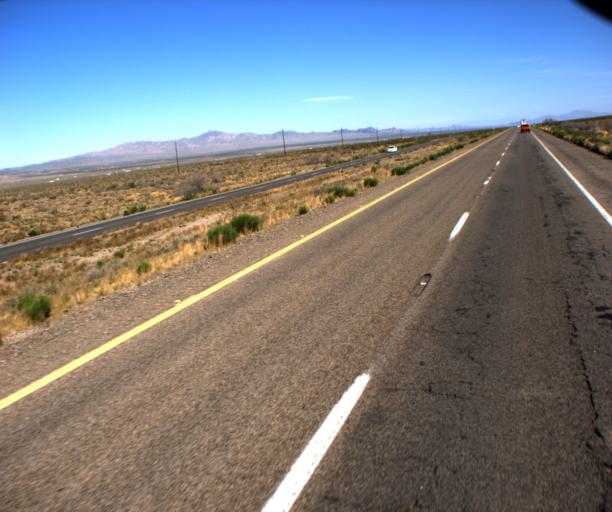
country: US
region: Arizona
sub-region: Mohave County
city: Dolan Springs
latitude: 35.4670
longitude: -114.3089
